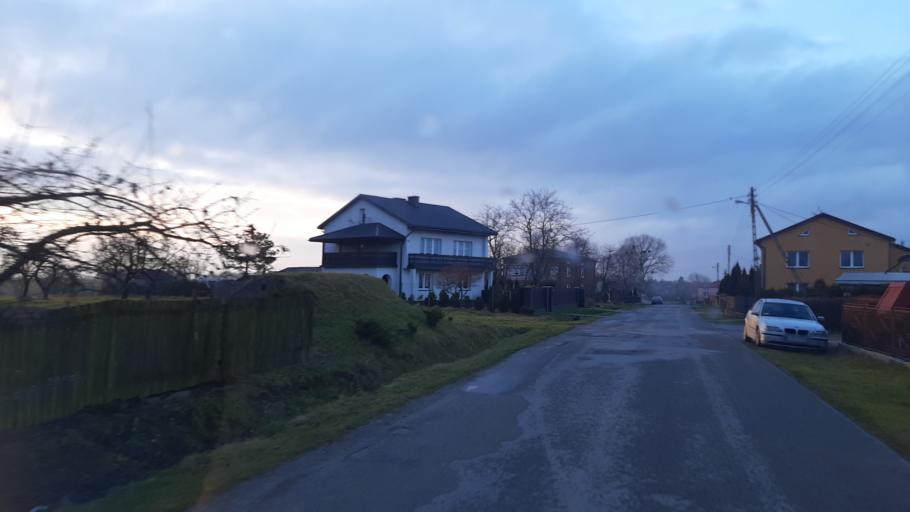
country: PL
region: Lublin Voivodeship
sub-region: Powiat lubelski
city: Garbow
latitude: 51.3810
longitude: 22.3946
